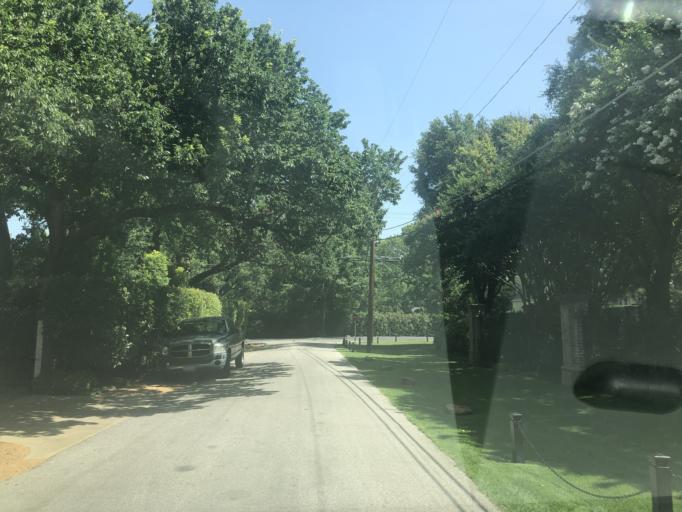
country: US
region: Texas
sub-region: Dallas County
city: University Park
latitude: 32.8734
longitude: -96.8158
